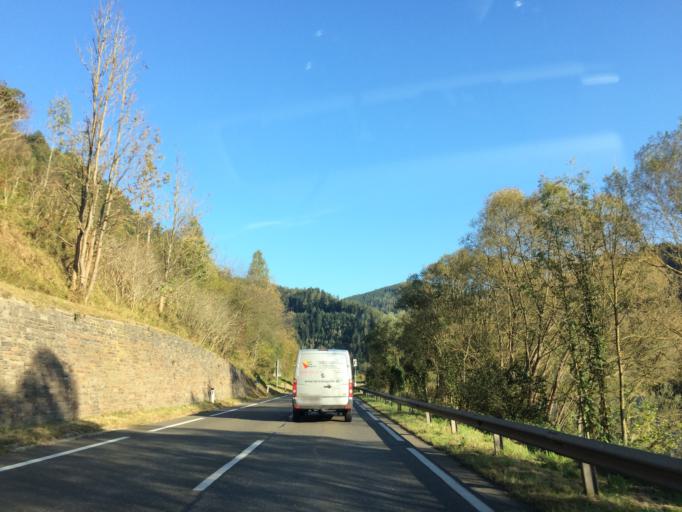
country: AT
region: Styria
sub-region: Politischer Bezirk Leoben
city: Sankt Michael in Obersteiermark
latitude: 47.3413
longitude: 15.0385
